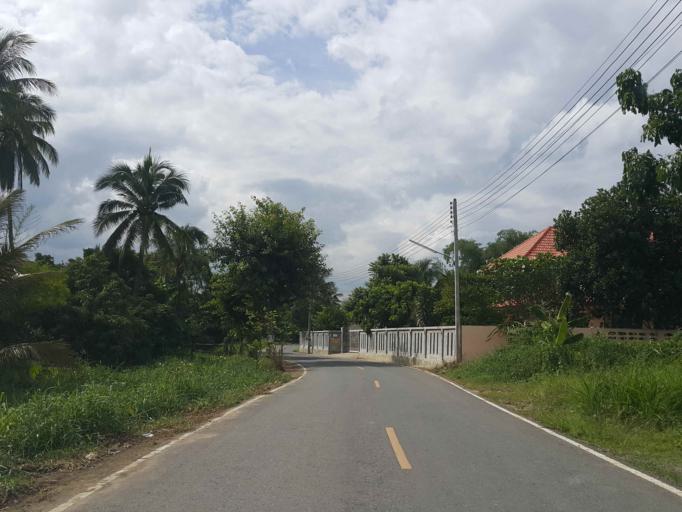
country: TH
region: Chiang Mai
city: Saraphi
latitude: 18.7343
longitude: 99.0589
